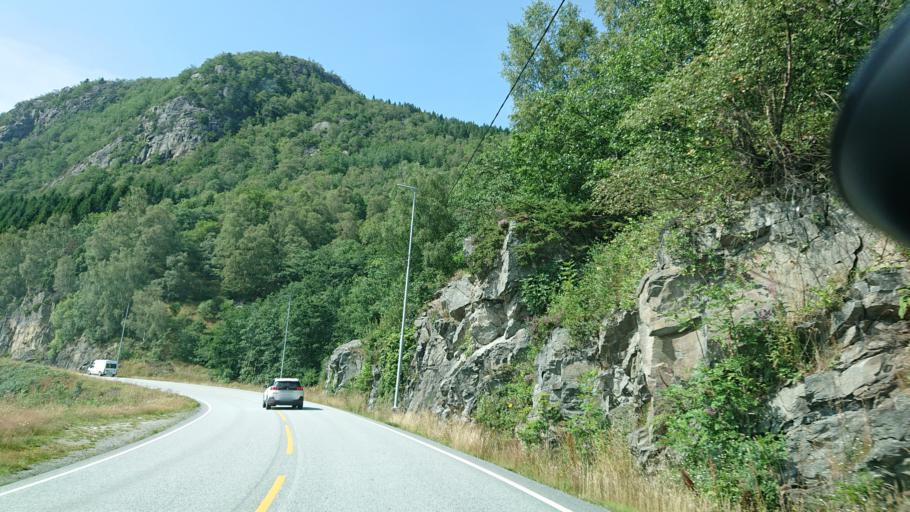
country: NO
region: Rogaland
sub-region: Strand
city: Tau
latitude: 59.0687
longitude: 5.9760
